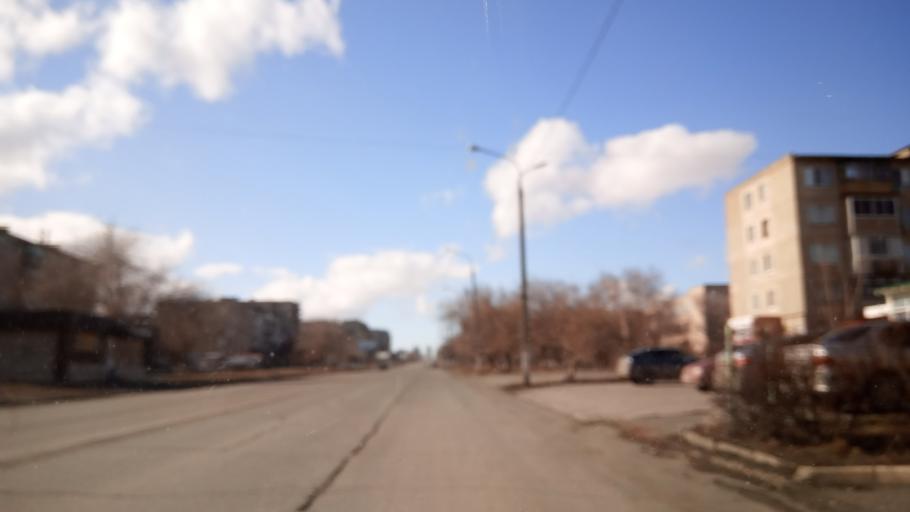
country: RU
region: Orenburg
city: Novotroitsk
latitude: 51.1838
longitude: 58.2830
